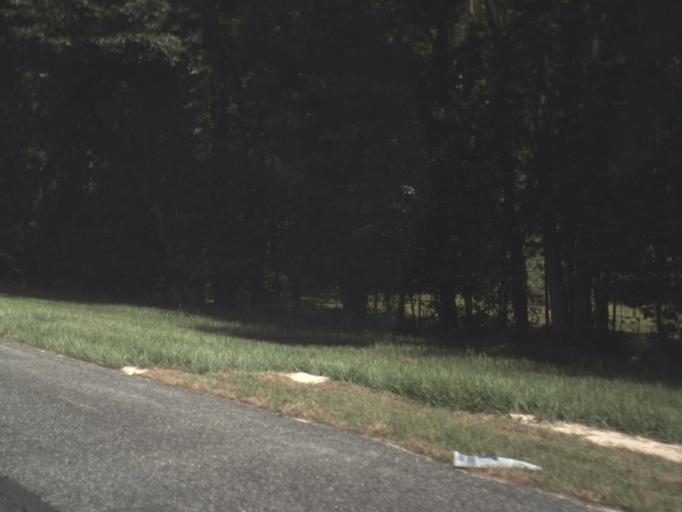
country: US
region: Florida
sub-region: Madison County
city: Madison
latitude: 30.4314
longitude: -83.6016
